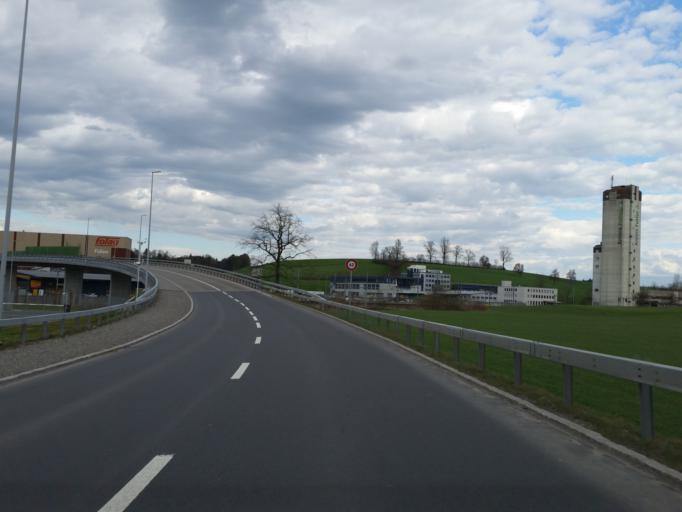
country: CH
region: Lucerne
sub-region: Sursee District
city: Neuenkirch
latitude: 47.1141
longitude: 8.2002
